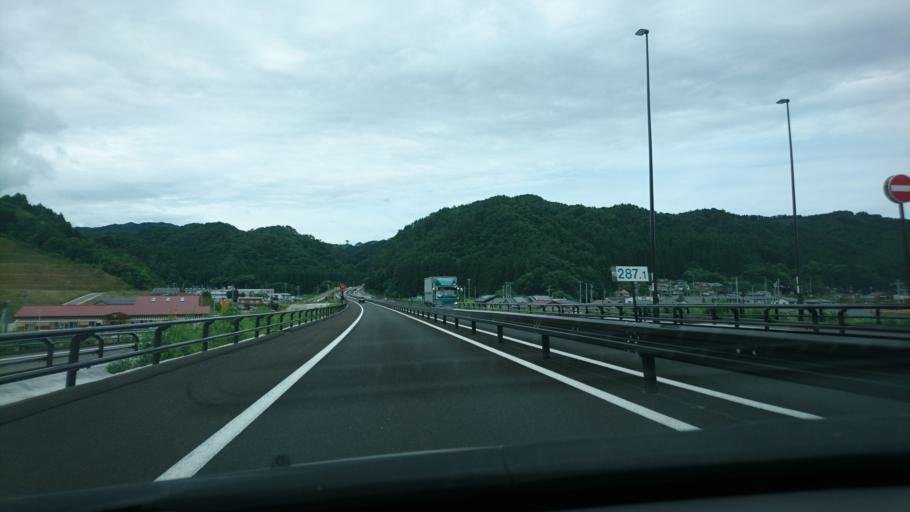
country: JP
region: Iwate
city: Miyako
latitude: 39.8397
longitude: 141.9577
